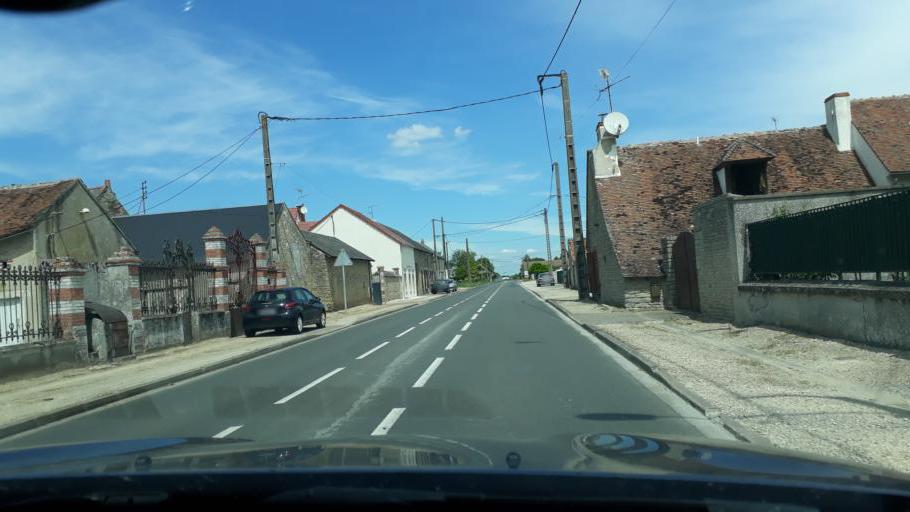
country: FR
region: Centre
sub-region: Departement du Loiret
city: Dadonville
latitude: 48.1032
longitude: 2.2448
